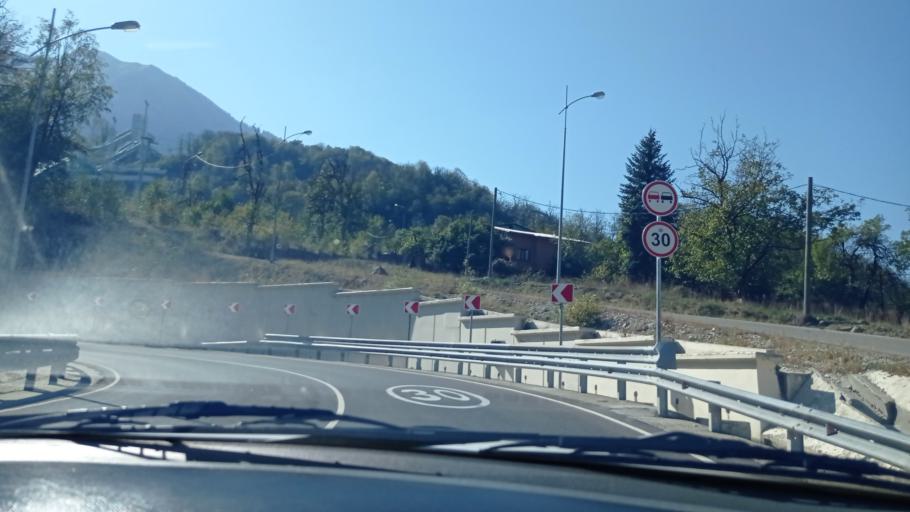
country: RU
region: Krasnodarskiy
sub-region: Sochi City
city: Krasnaya Polyana
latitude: 43.6814
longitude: 40.2422
